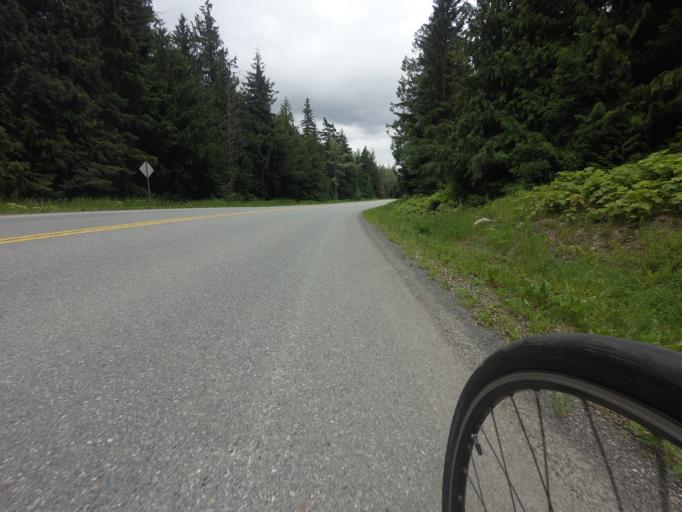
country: CA
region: British Columbia
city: Lillooet
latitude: 50.5305
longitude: -122.1561
